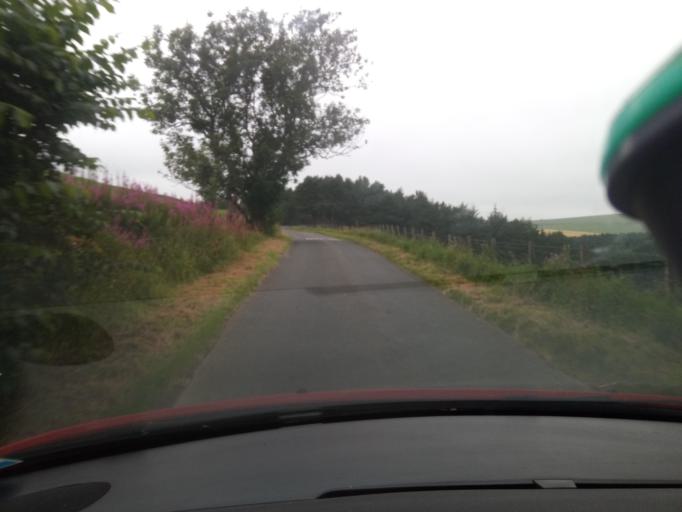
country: GB
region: Scotland
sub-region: The Scottish Borders
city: Galashiels
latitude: 55.7288
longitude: -2.8960
